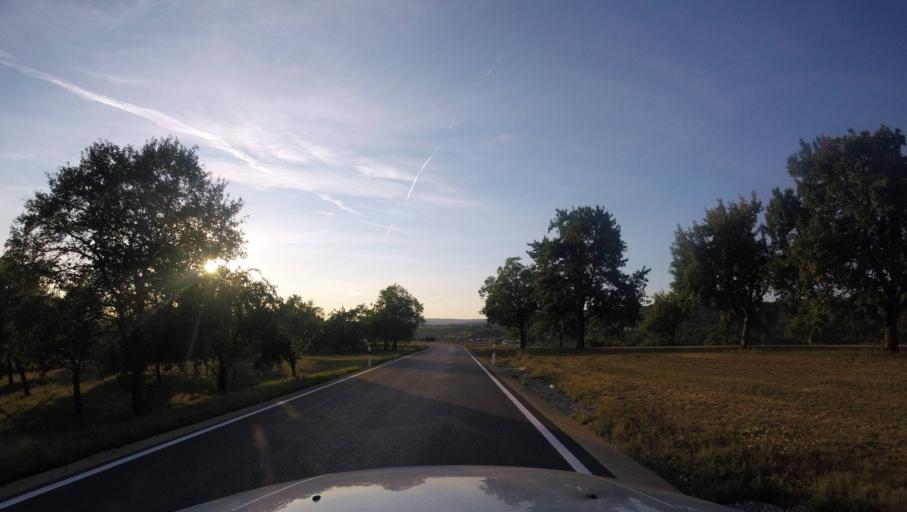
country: DE
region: Baden-Wuerttemberg
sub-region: Regierungsbezirk Stuttgart
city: Rudersberg
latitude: 48.9217
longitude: 9.5330
